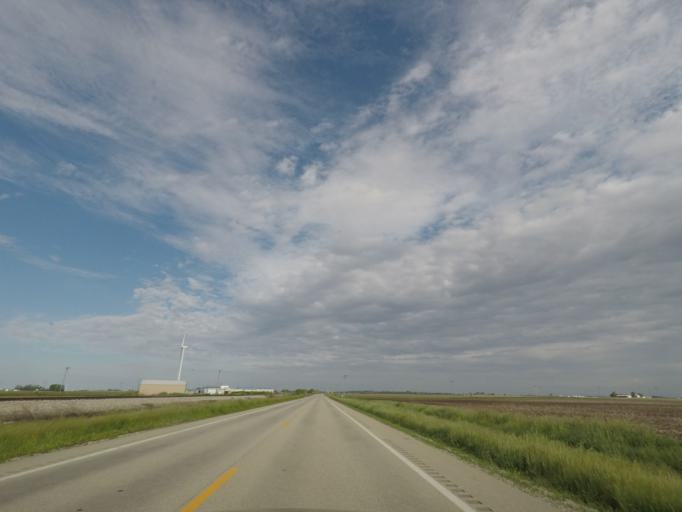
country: US
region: Illinois
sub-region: Logan County
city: Mount Pulaski
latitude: 39.9921
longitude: -89.2452
